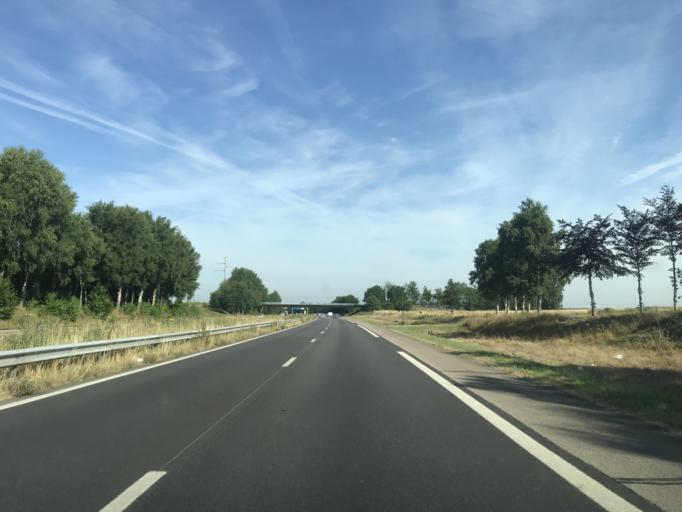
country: FR
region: Haute-Normandie
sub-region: Departement de la Seine-Maritime
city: Roumare
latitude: 49.5119
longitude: 0.9859
